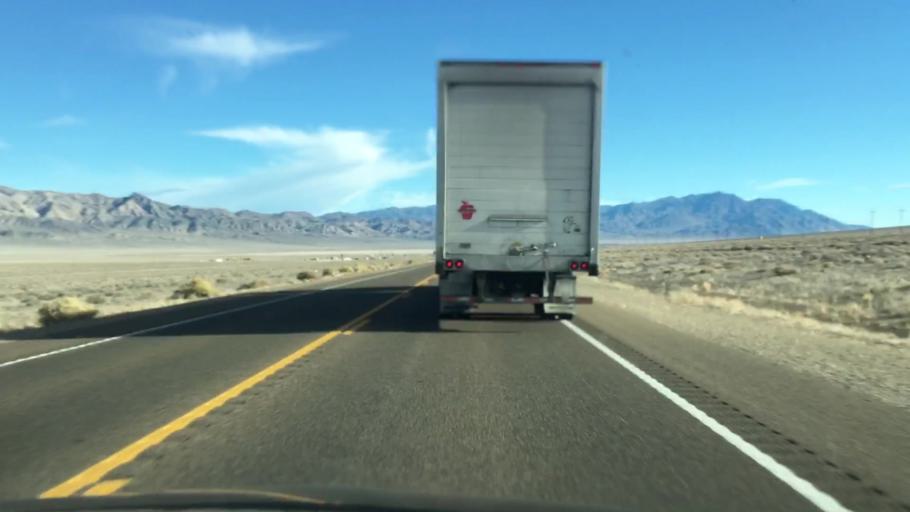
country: US
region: Nevada
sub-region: Mineral County
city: Hawthorne
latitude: 38.5209
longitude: -118.2094
